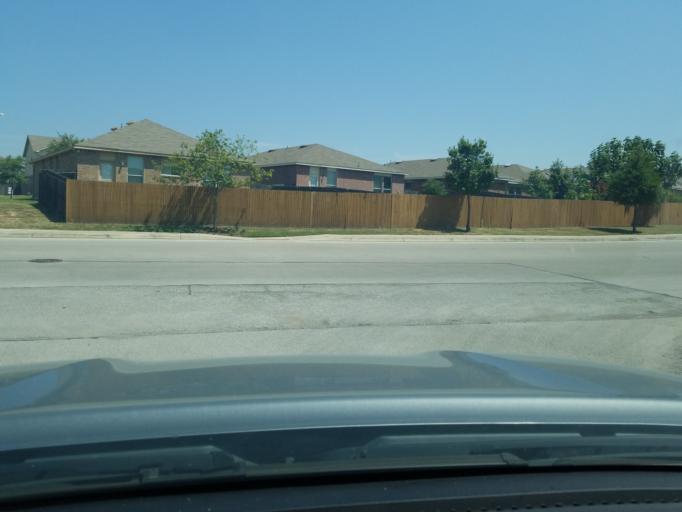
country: US
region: Texas
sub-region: Bexar County
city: Timberwood Park
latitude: 29.7023
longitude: -98.4806
